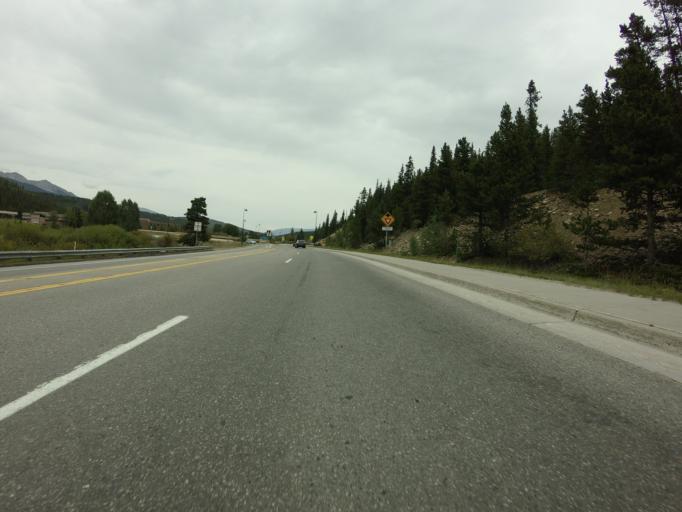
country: US
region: Colorado
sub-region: Summit County
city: Breckenridge
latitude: 39.4893
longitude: -106.0456
